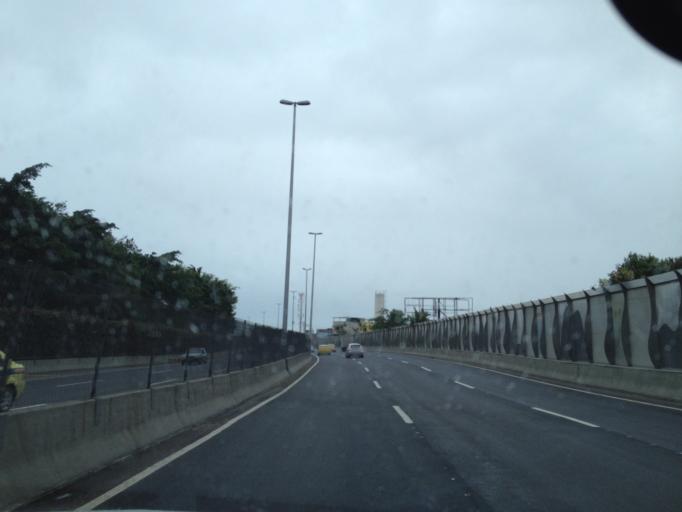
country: BR
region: Rio de Janeiro
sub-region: Sao Joao De Meriti
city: Sao Joao de Meriti
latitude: -22.9489
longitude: -43.3561
